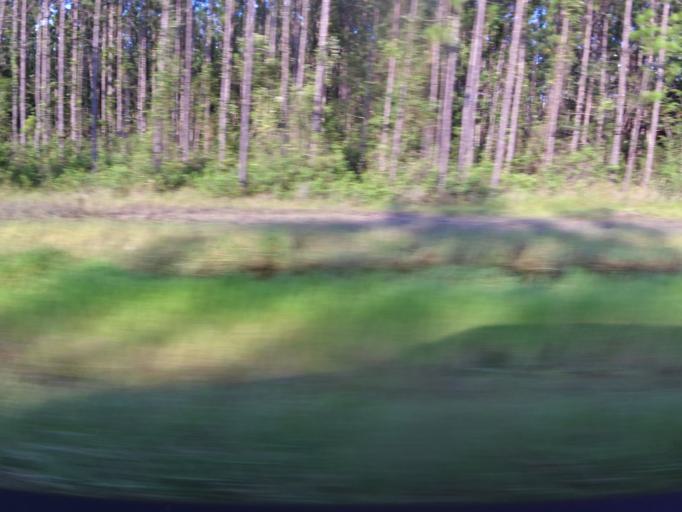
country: US
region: Florida
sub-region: Duval County
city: Baldwin
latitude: 30.3926
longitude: -82.0300
